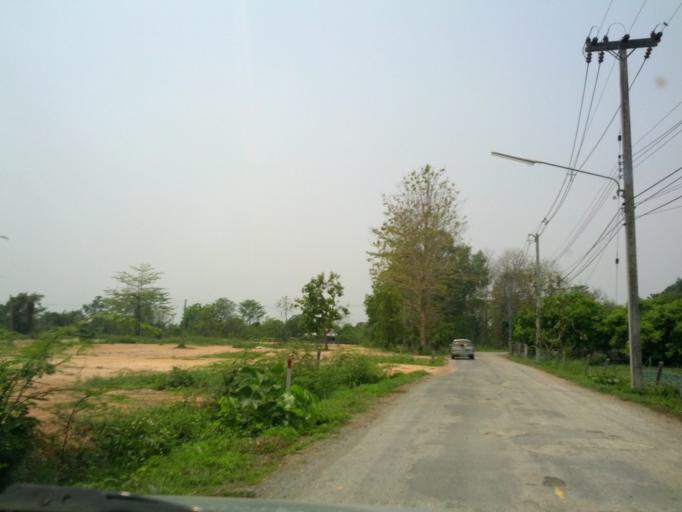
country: TH
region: Chiang Mai
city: San Sai
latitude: 18.8950
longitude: 99.0767
